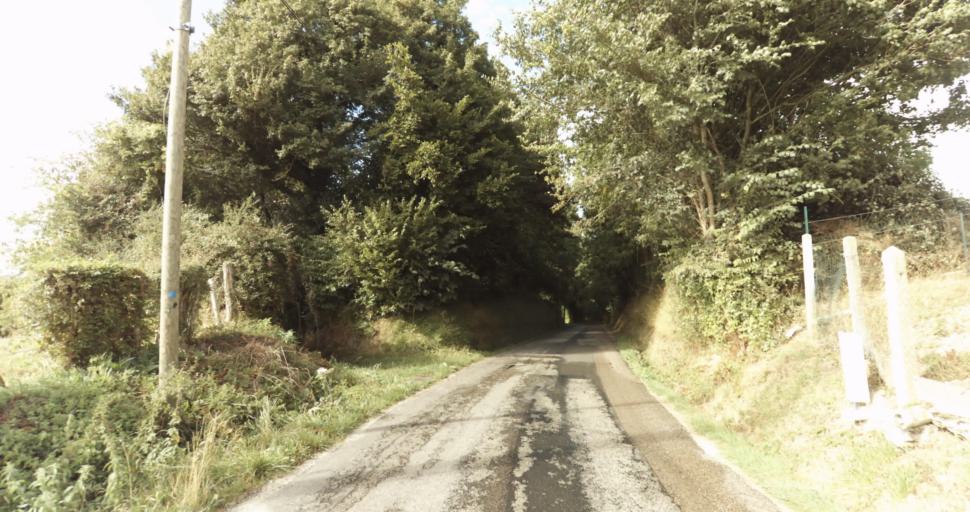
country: FR
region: Lower Normandy
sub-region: Departement de l'Orne
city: Gace
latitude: 48.7923
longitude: 0.3016
